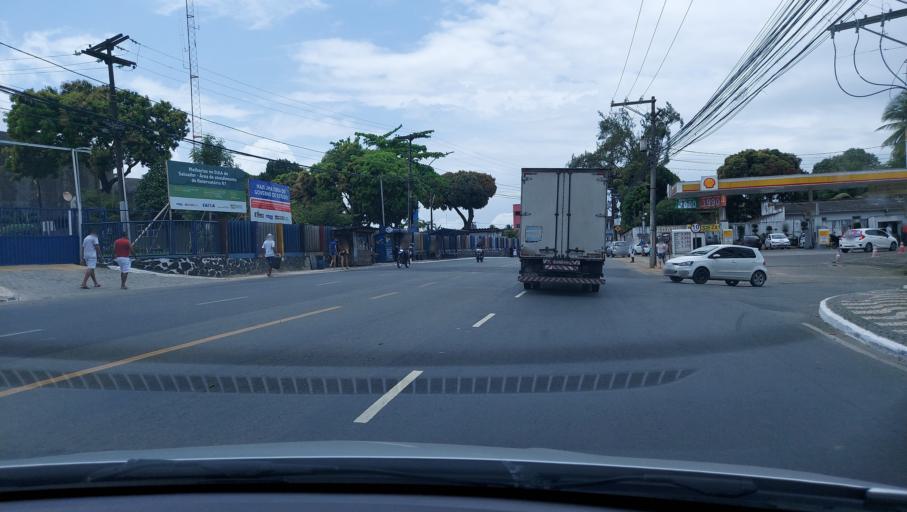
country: BR
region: Bahia
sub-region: Salvador
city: Salvador
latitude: -12.9546
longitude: -38.4638
